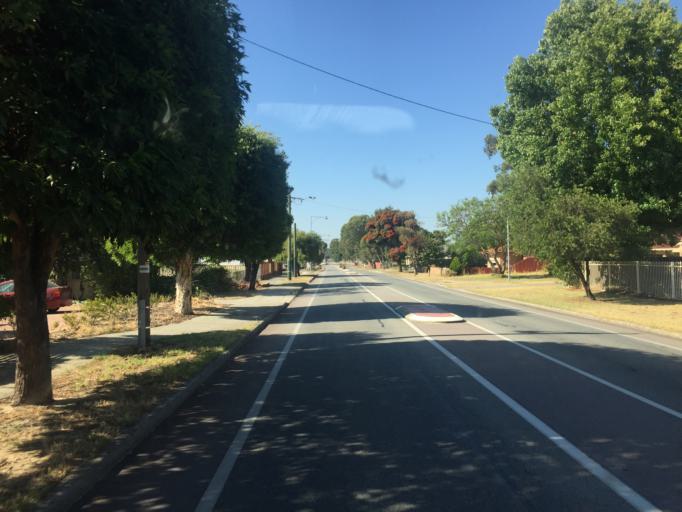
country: AU
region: Western Australia
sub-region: Gosnells
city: Maddington
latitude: -32.0356
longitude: 115.9821
